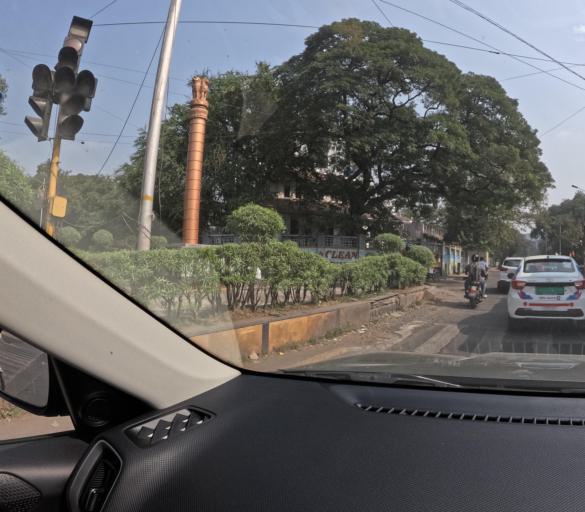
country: IN
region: Maharashtra
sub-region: Pune Division
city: Pune
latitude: 18.5255
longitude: 73.8676
